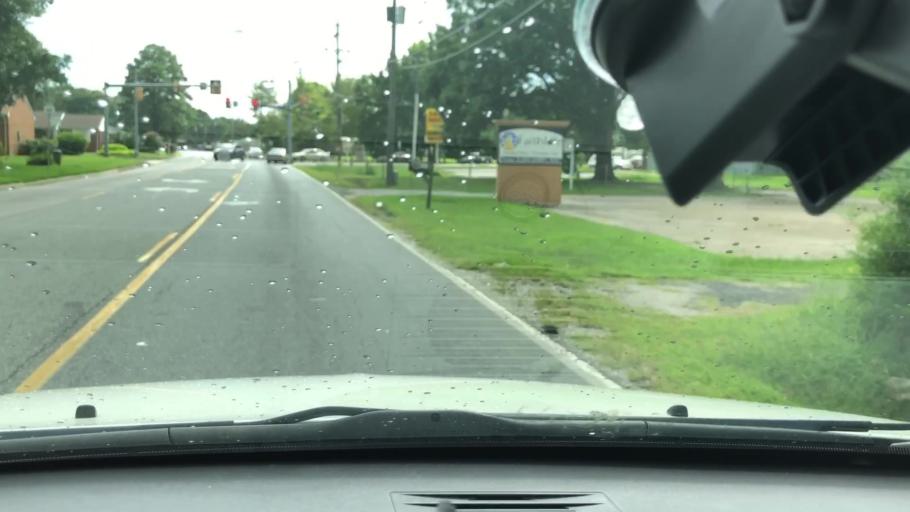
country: US
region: Virginia
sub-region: City of Chesapeake
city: Chesapeake
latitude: 36.7864
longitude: -76.2658
